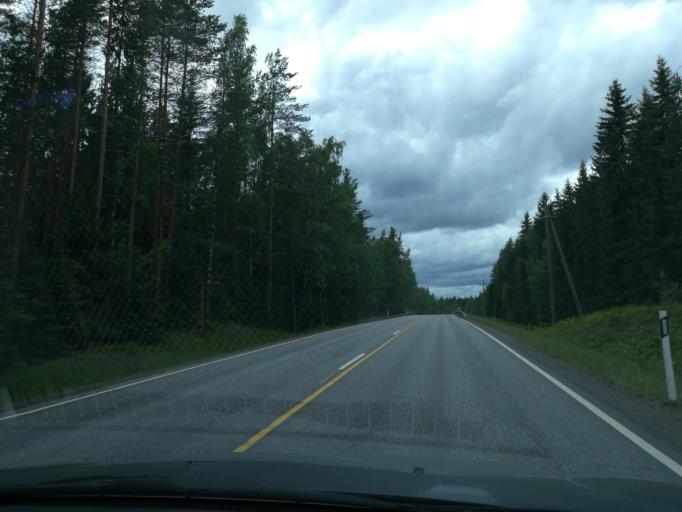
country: FI
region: South Karelia
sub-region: Lappeenranta
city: Taipalsaari
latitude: 61.0607
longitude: 27.9938
